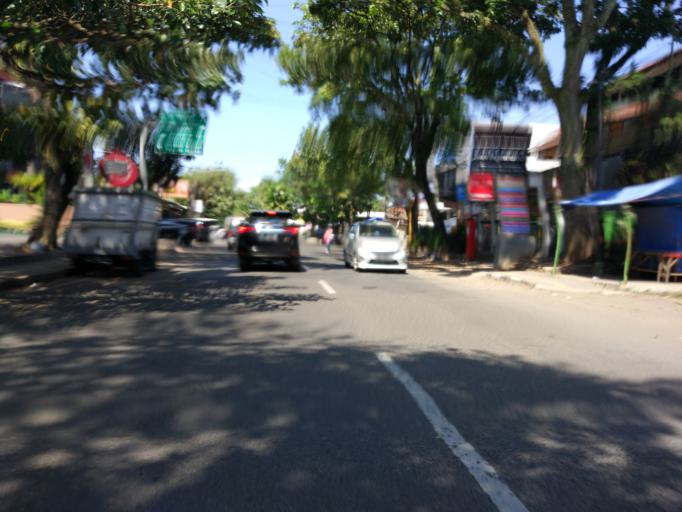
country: ID
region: West Java
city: Bandung
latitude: -6.9271
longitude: 107.6195
